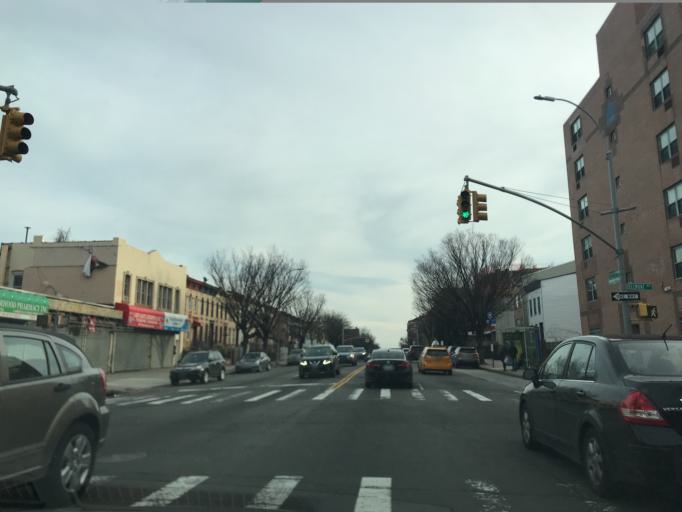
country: US
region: New York
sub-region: Kings County
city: East New York
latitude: 40.6709
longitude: -73.8956
